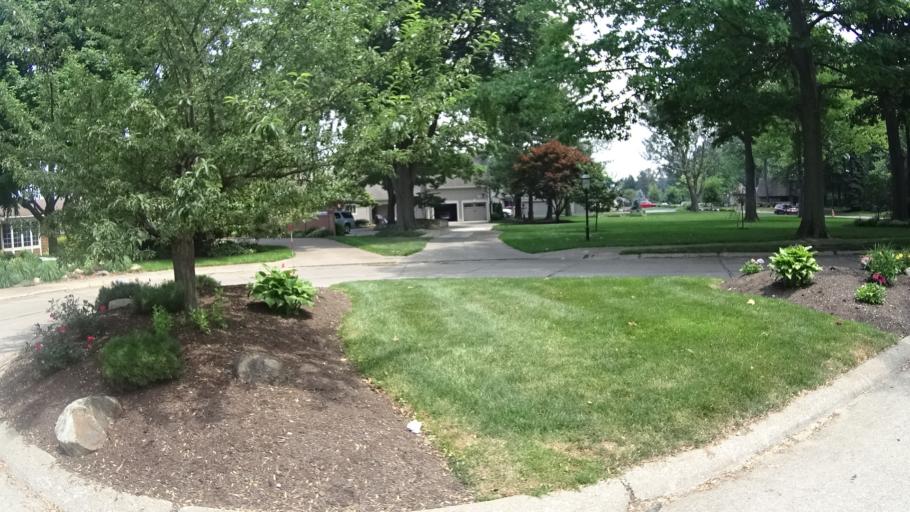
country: US
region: Ohio
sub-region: Erie County
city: Huron
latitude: 41.3887
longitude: -82.5290
